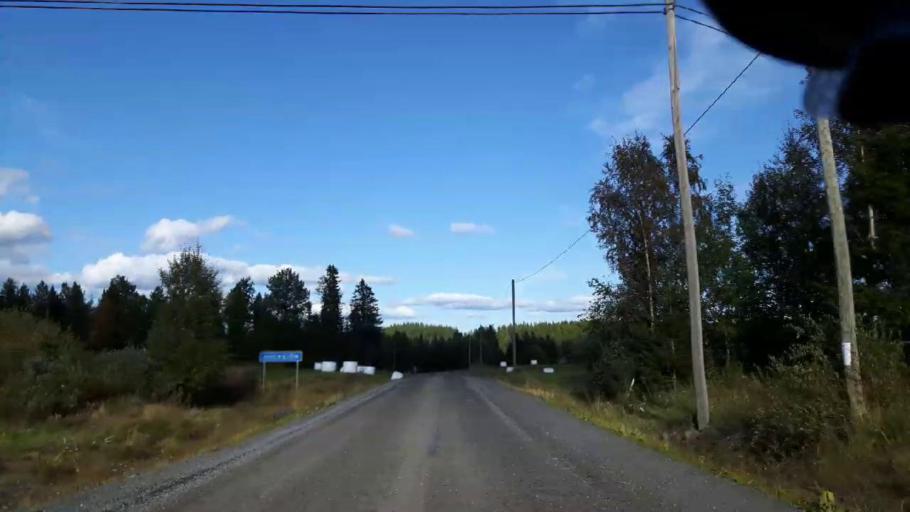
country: SE
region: Jaemtland
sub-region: Ragunda Kommun
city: Hammarstrand
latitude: 63.4342
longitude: 16.1848
